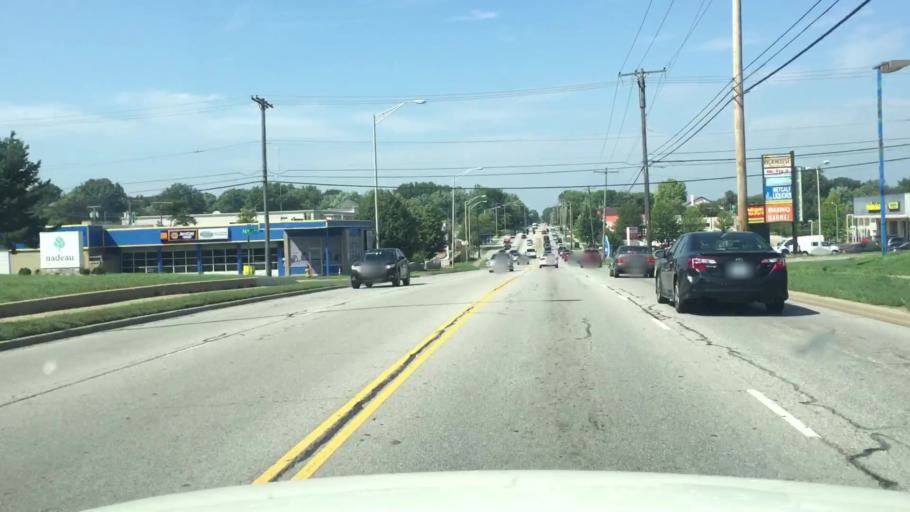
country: US
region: Kansas
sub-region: Johnson County
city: Overland Park
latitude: 38.9910
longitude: -94.6677
